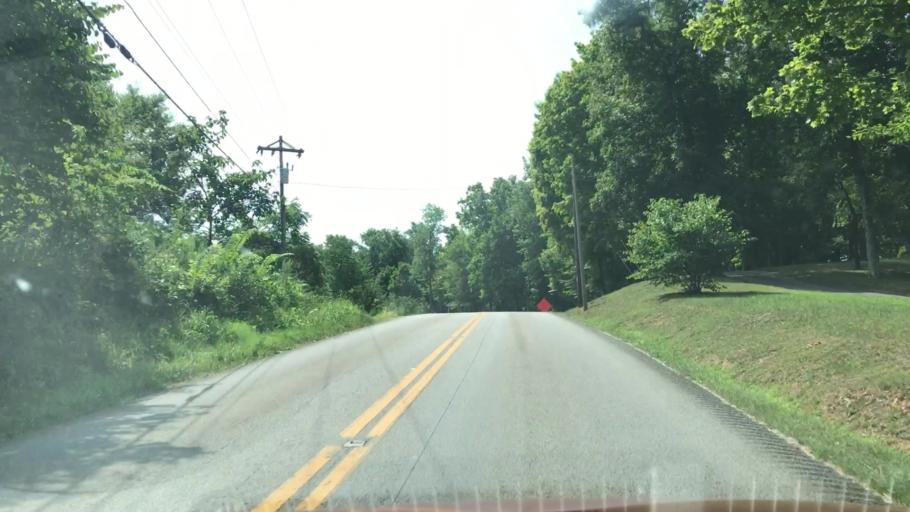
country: US
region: Kentucky
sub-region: Barren County
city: Glasgow
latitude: 36.9006
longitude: -85.8634
